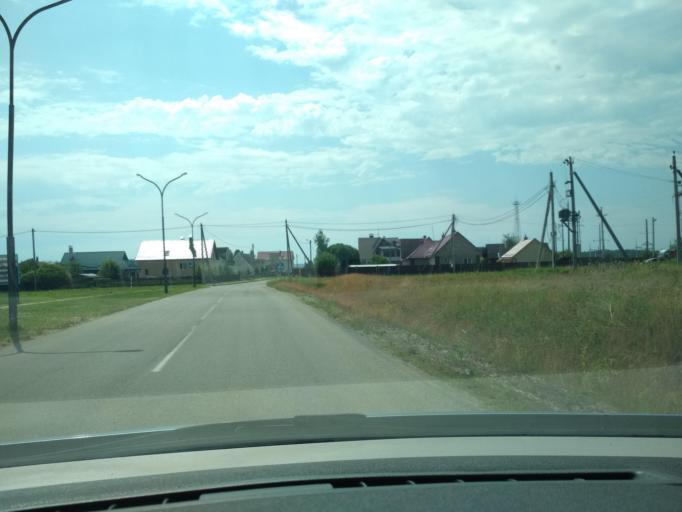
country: BY
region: Grodnenskaya
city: Astravyets
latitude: 54.6233
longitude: 25.9563
